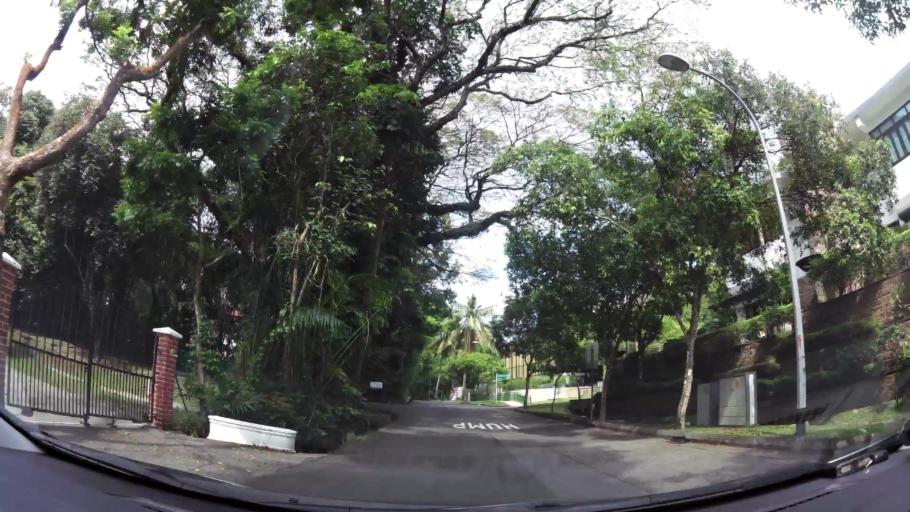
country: SG
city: Singapore
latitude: 1.3007
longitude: 103.8148
